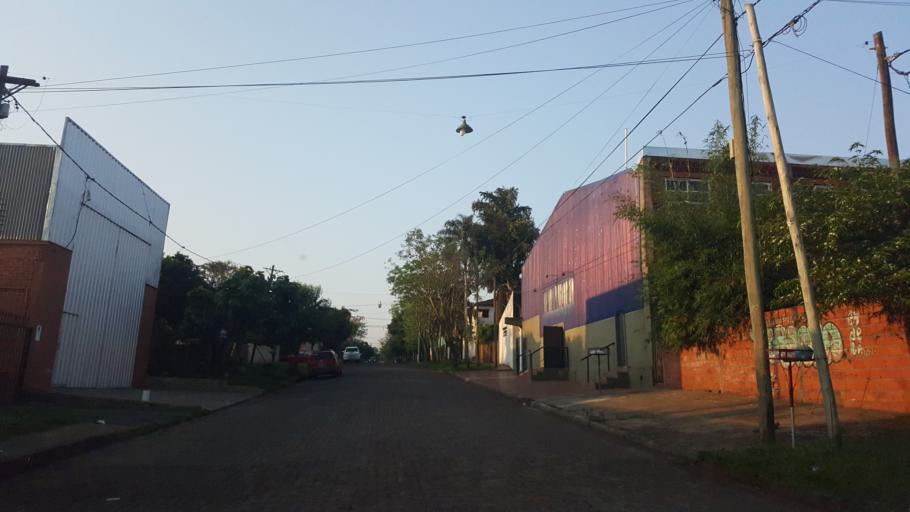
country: AR
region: Misiones
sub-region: Departamento de Capital
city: Posadas
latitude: -27.3968
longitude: -55.9038
